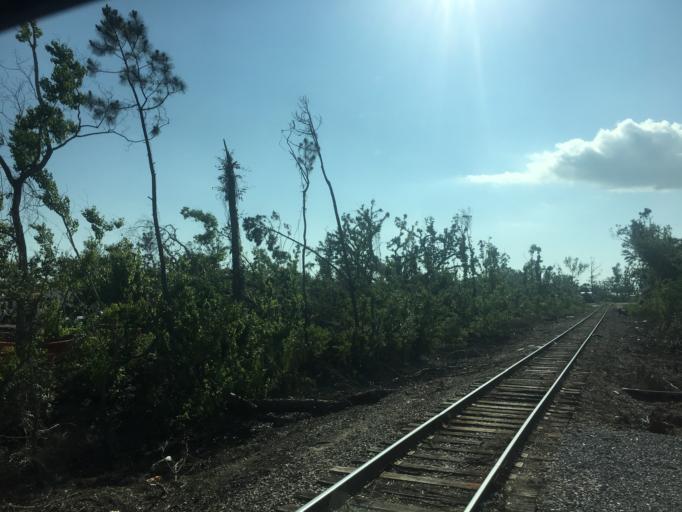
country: US
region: Florida
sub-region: Bay County
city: Cedar Grove
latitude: 30.1607
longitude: -85.6209
